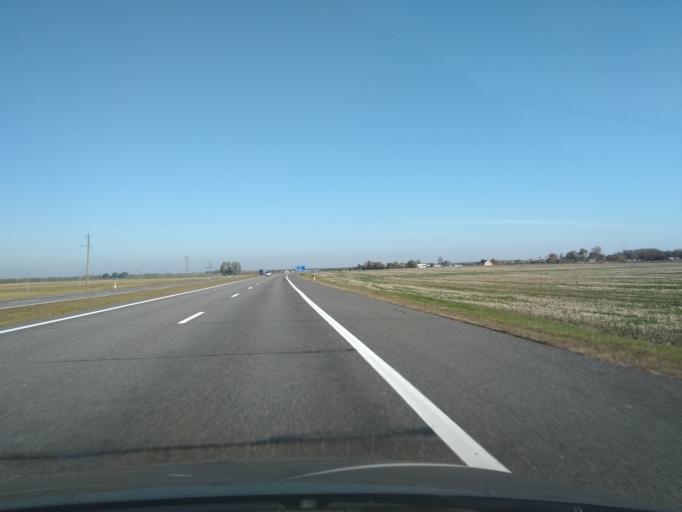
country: BY
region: Brest
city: Byaroza
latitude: 52.4832
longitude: 24.9545
